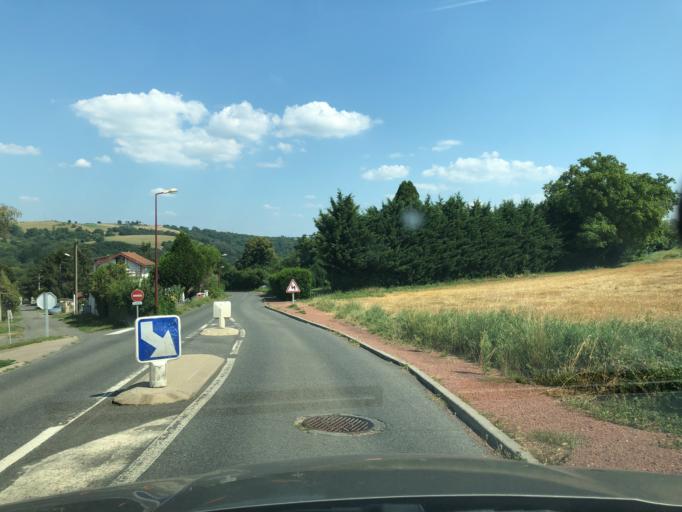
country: FR
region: Auvergne
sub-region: Departement de l'Allier
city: Cusset
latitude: 46.1173
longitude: 3.4642
